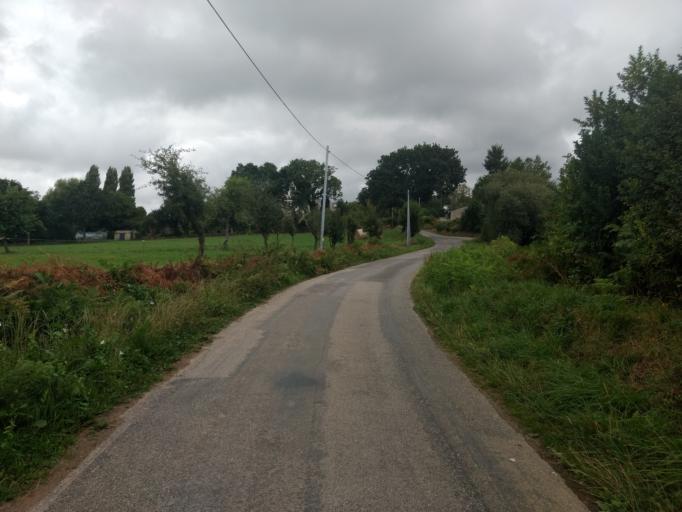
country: FR
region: Brittany
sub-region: Departement du Finistere
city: Loperhet
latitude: 48.3608
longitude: -4.3024
